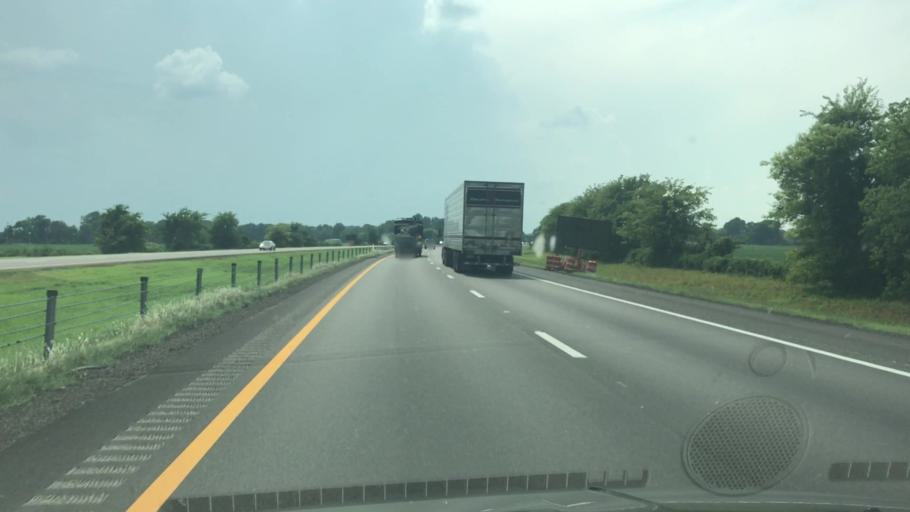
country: US
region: Arkansas
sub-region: Crittenden County
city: Earle
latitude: 35.1350
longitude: -90.4370
